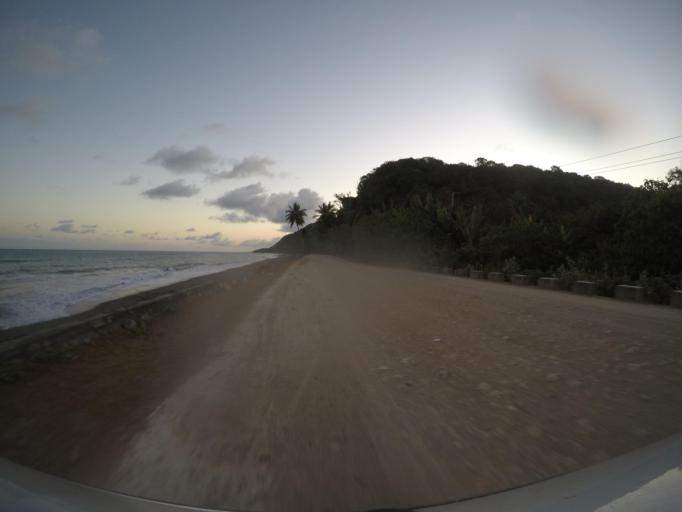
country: TL
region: Viqueque
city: Viqueque
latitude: -8.7855
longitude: 126.6352
